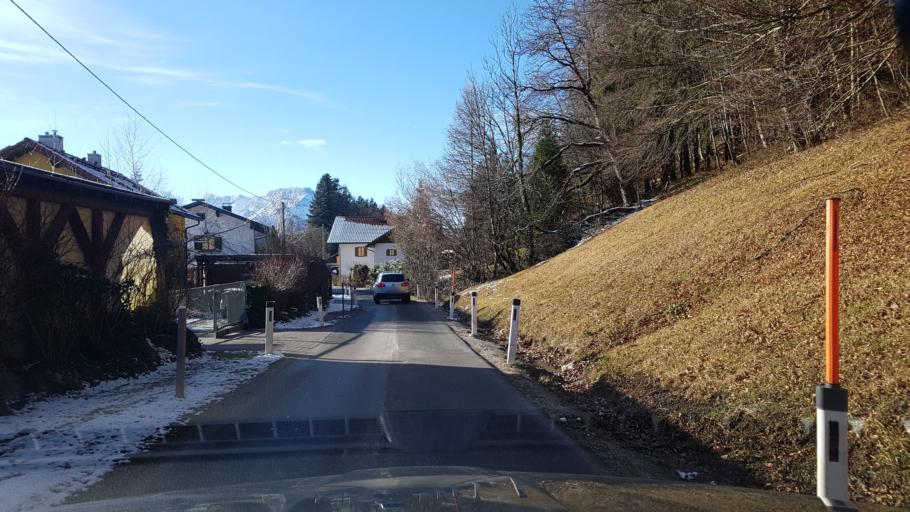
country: AT
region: Salzburg
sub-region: Politischer Bezirk Salzburg-Umgebung
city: Koppl
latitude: 47.7753
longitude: 13.1322
